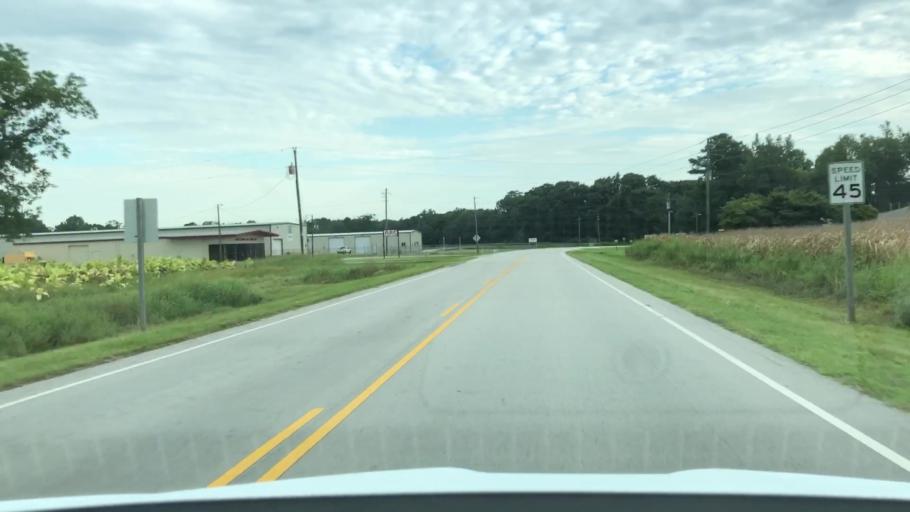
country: US
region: North Carolina
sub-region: Jones County
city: Trenton
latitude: 35.0548
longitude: -77.3567
